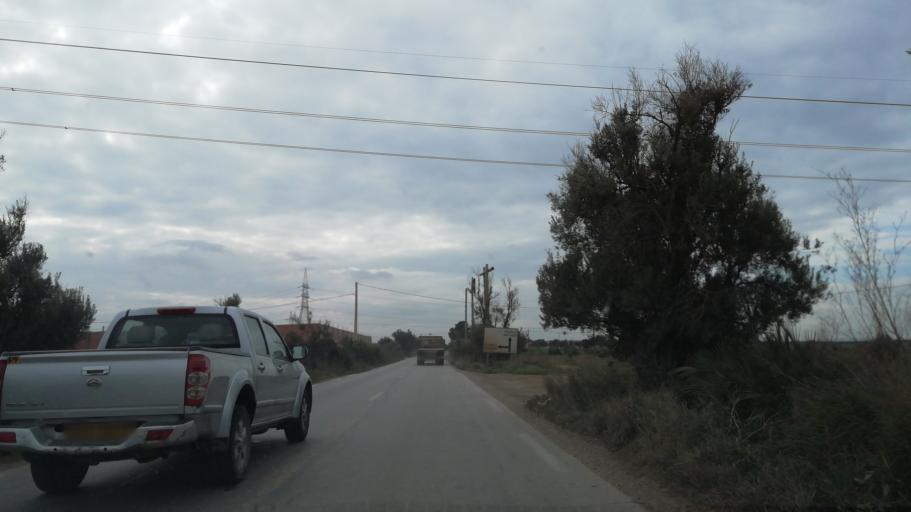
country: DZ
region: Oran
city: Ain el Bya
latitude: 35.7735
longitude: -0.3466
